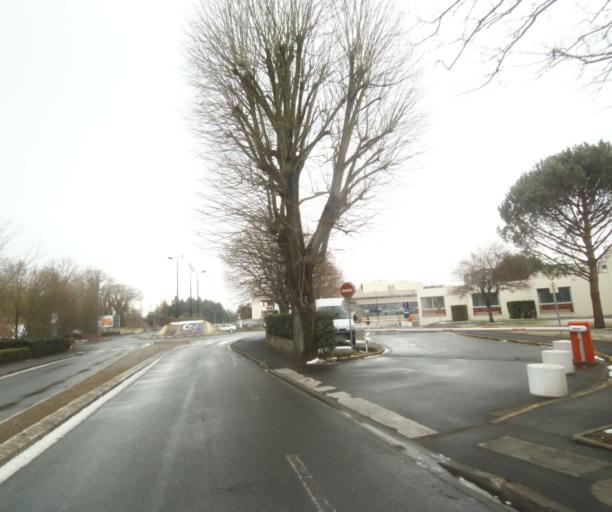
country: FR
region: Poitou-Charentes
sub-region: Departement des Deux-Sevres
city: Niort
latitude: 46.3167
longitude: -0.4577
